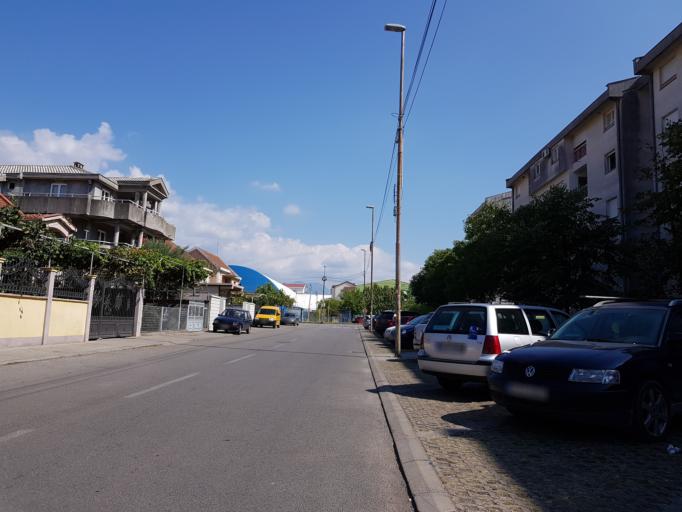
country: ME
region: Podgorica
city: Podgorica
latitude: 42.4287
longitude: 19.2752
